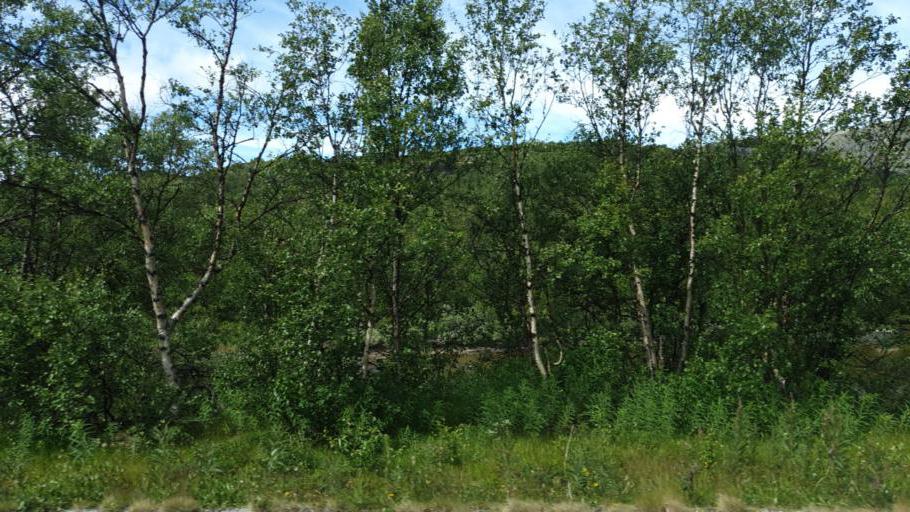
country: NO
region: Oppland
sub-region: Oystre Slidre
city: Heggenes
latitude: 61.4947
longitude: 8.8440
